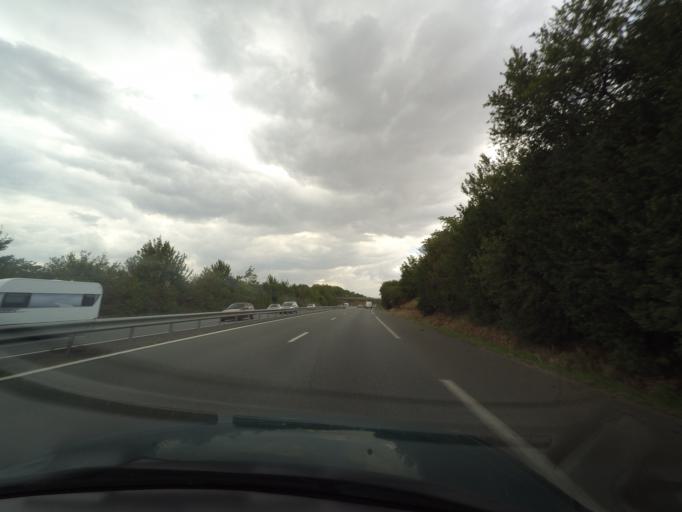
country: FR
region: Poitou-Charentes
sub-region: Departement de la Vienne
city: Migne-Auxances
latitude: 46.6201
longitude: 0.3054
